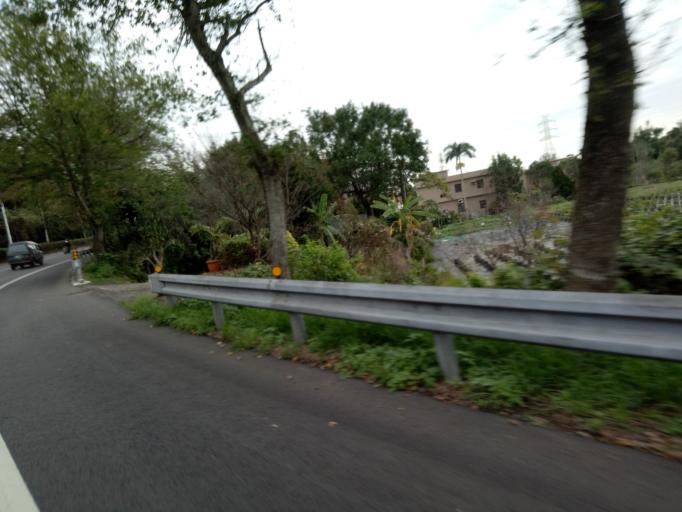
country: TW
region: Taiwan
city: Daxi
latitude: 24.8758
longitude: 121.2502
